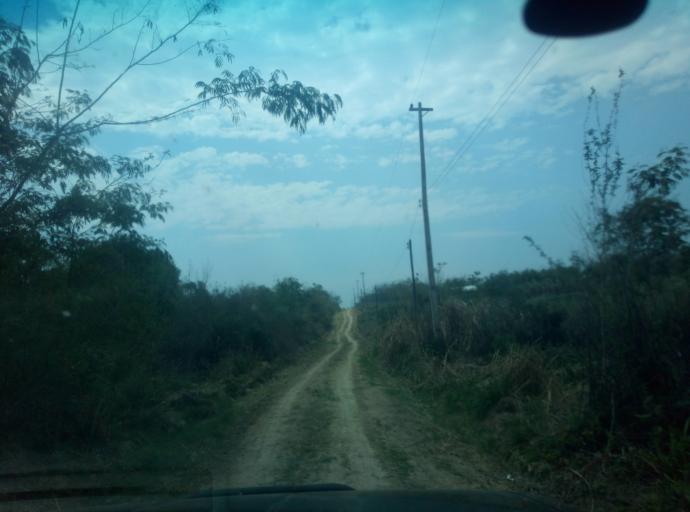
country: PY
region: Caaguazu
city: Doctor Cecilio Baez
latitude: -25.1384
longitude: -56.1635
